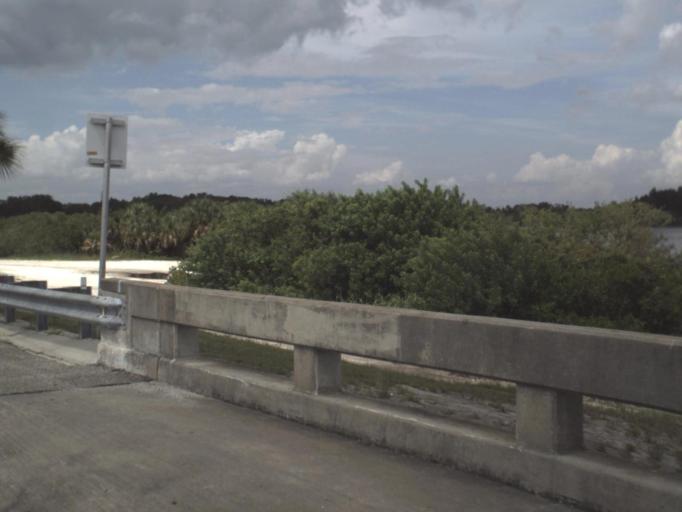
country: US
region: Florida
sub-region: Manatee County
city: Memphis
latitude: 27.5683
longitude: -82.5690
